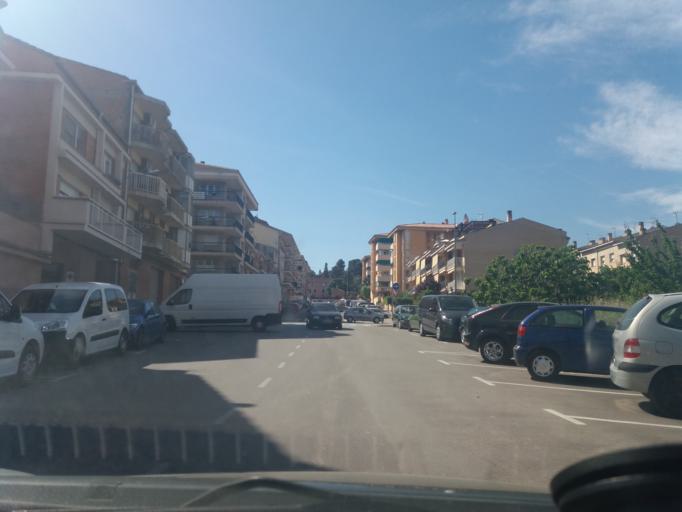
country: ES
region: Catalonia
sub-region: Provincia de Barcelona
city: Manresa
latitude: 41.7390
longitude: 1.8359
